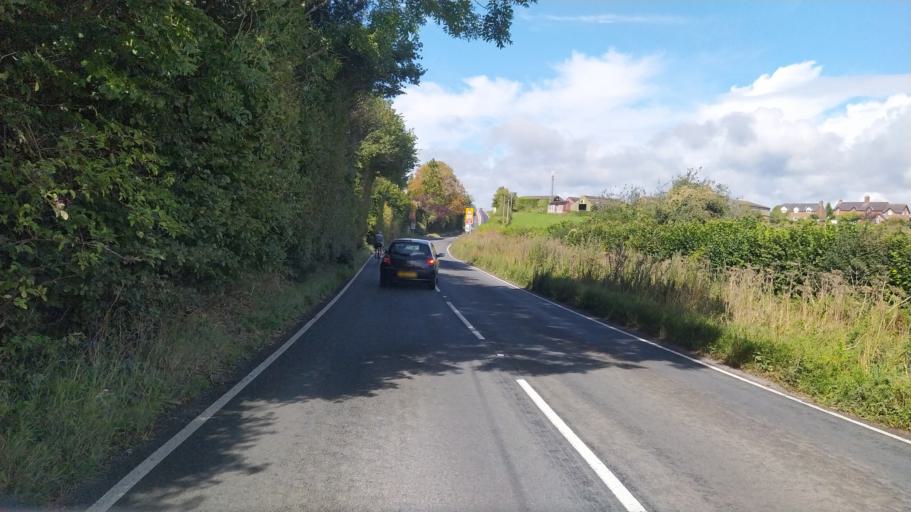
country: GB
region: England
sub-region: Dorset
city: Blandford Forum
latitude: 50.8884
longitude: -2.2217
